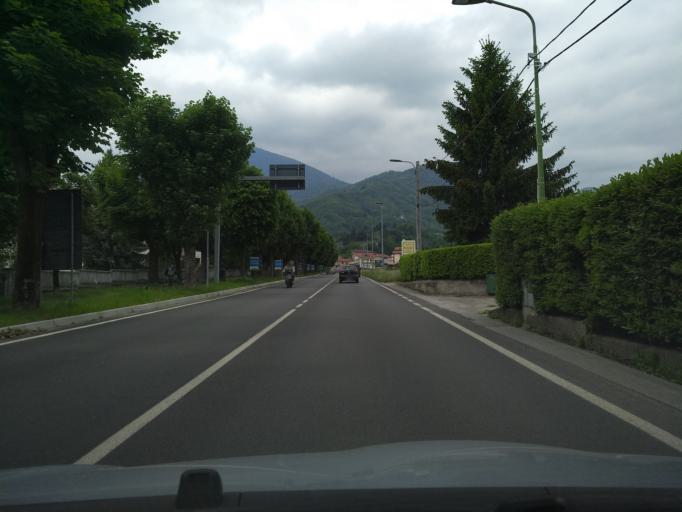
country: IT
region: Piedmont
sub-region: Provincia di Torino
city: Luserna
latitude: 44.8183
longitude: 7.2360
